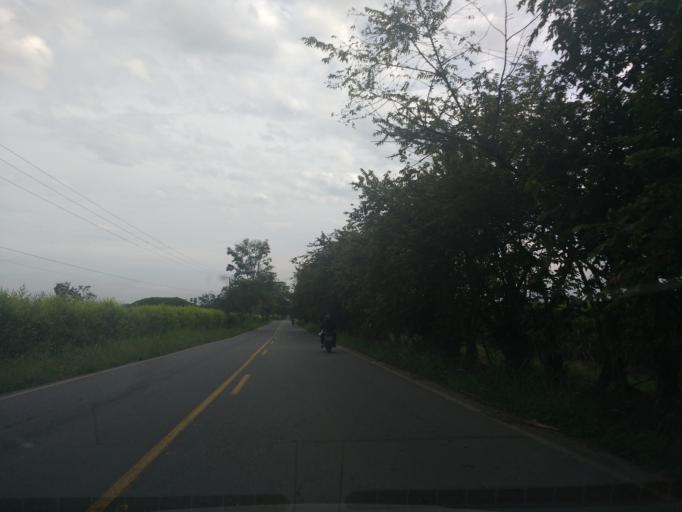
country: CO
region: Valle del Cauca
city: Florida
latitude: 3.3011
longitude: -76.2316
